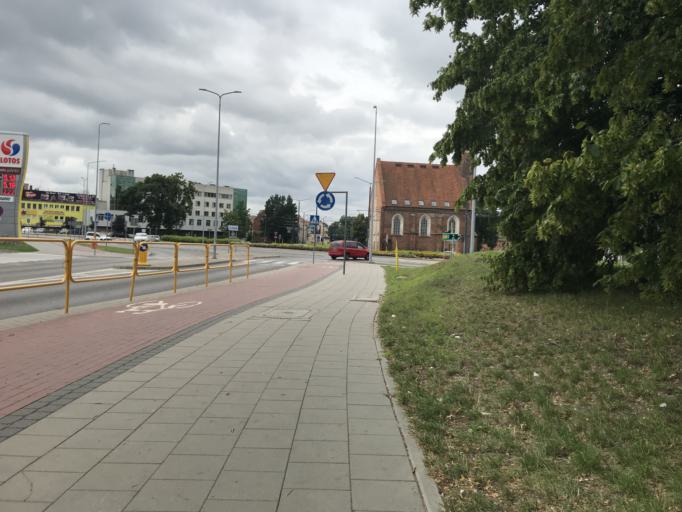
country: PL
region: Warmian-Masurian Voivodeship
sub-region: Powiat elblaski
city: Elblag
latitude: 54.1665
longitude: 19.3997
